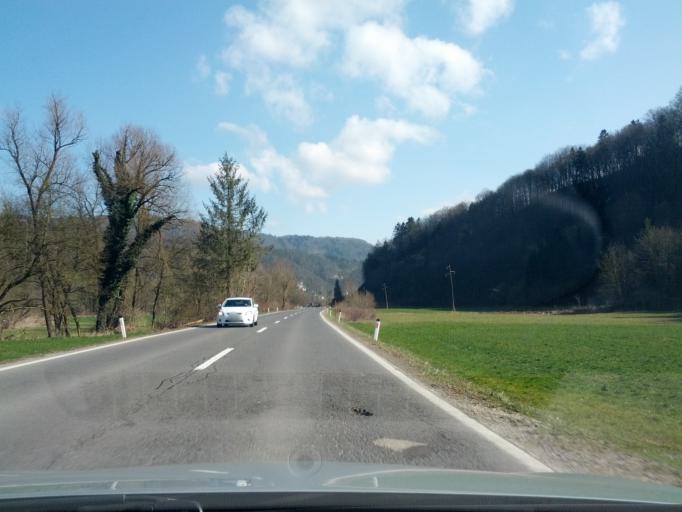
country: SI
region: Smartno pri Litiji
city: Smartno pri Litiji
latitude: 46.0784
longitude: 14.8731
